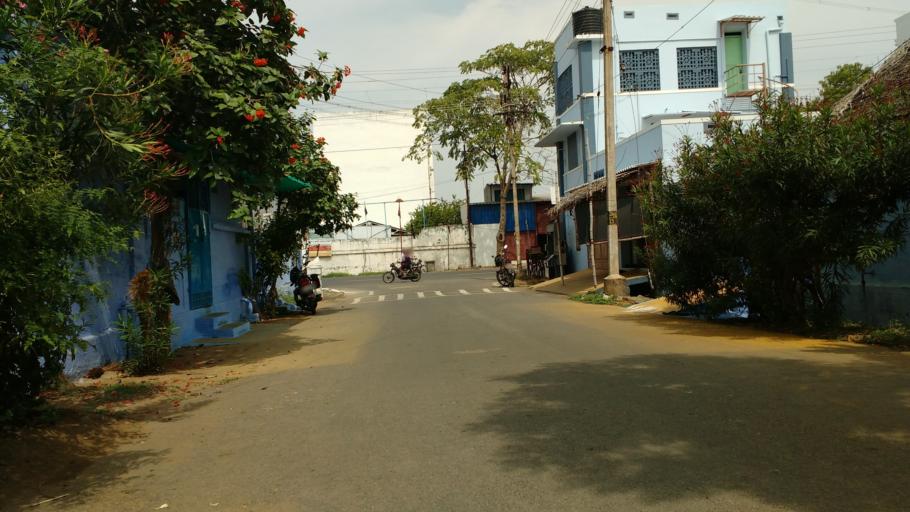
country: IN
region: Tamil Nadu
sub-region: Erode
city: Gobichettipalayam
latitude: 11.4541
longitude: 77.4446
